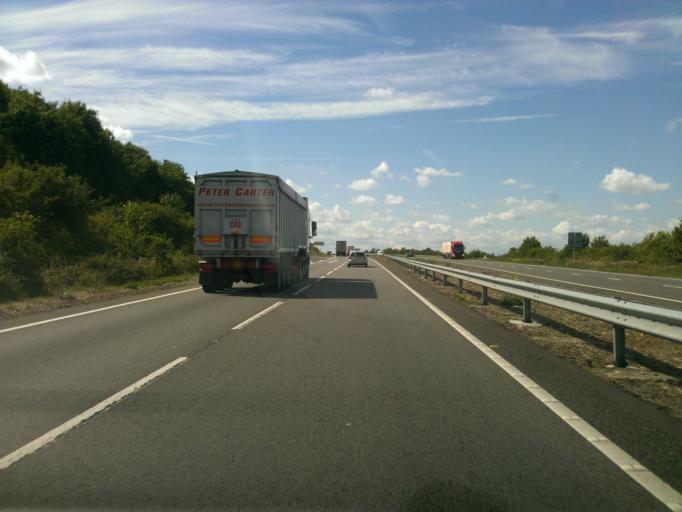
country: GB
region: England
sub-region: Bedford
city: Pertenhall
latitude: 52.3514
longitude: -0.3734
